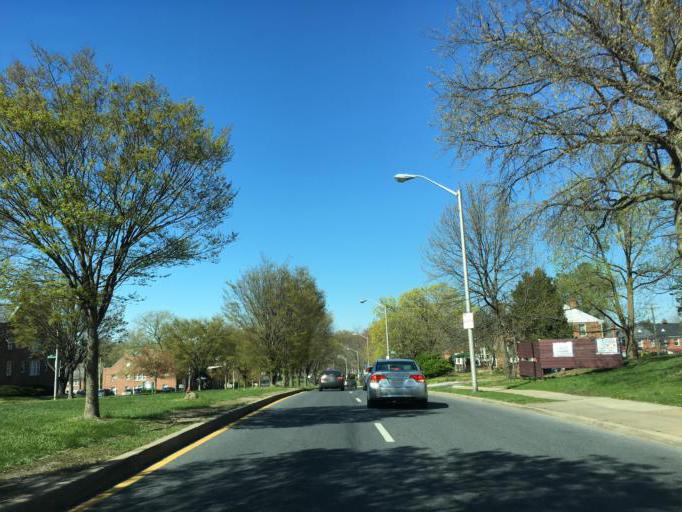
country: US
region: Maryland
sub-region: City of Baltimore
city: Baltimore
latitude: 39.3416
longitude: -76.5931
